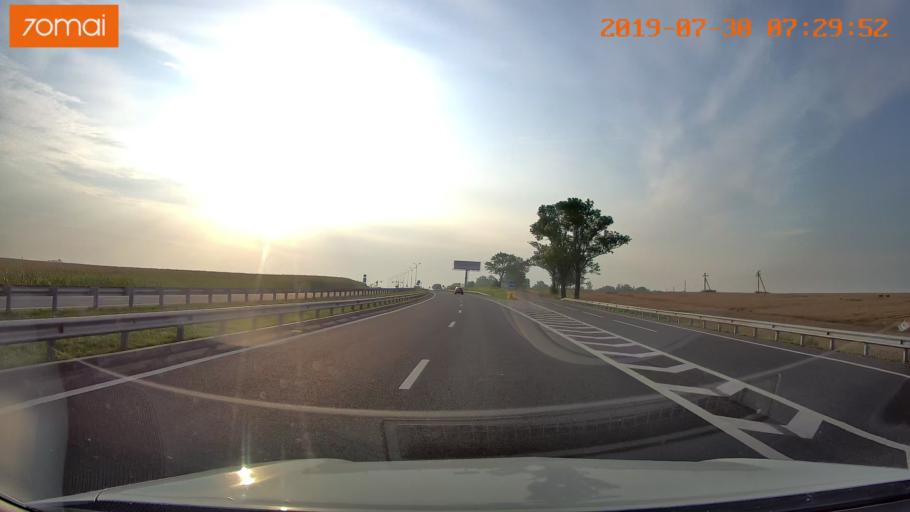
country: RU
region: Kaliningrad
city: Gvardeysk
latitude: 54.6704
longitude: 20.9509
